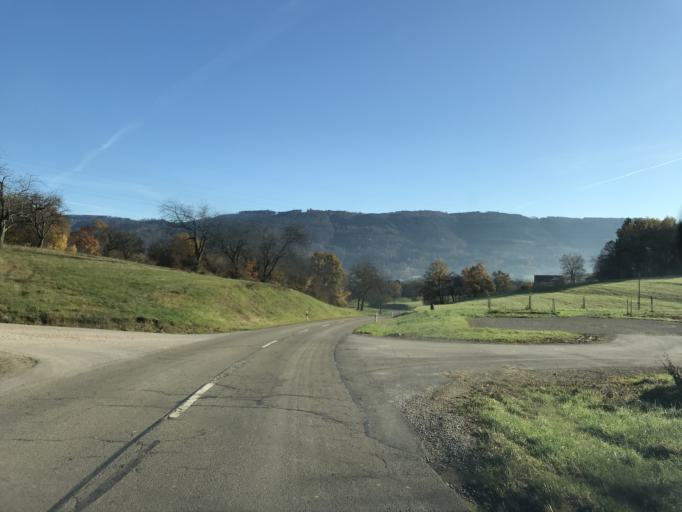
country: DE
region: Baden-Wuerttemberg
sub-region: Freiburg Region
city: Wehr
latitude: 47.6254
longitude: 7.8859
